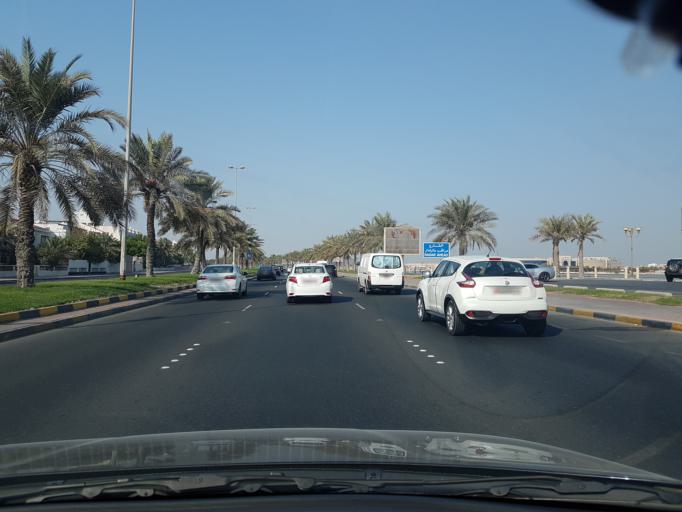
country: BH
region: Muharraq
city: Al Muharraq
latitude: 26.2494
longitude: 50.6202
